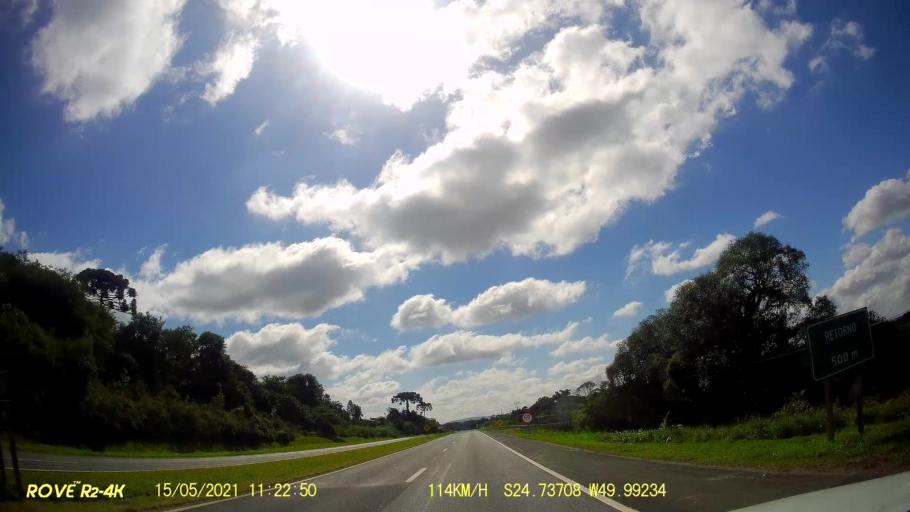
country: BR
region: Parana
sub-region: Castro
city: Castro
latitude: -24.7372
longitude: -49.9924
